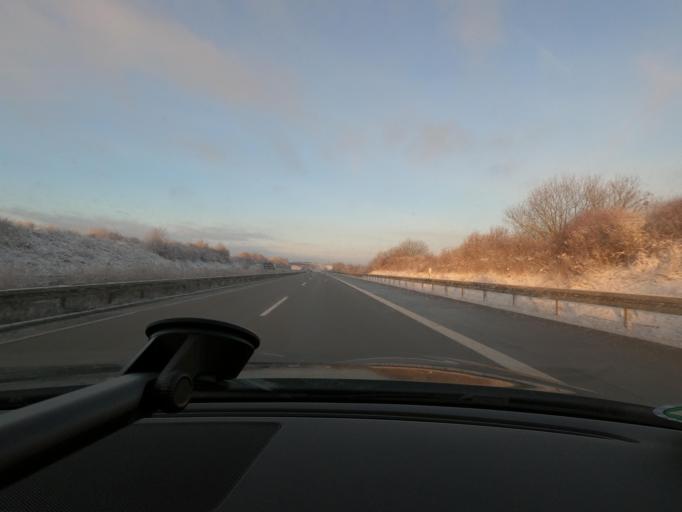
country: DE
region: Thuringia
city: Wingerode
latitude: 51.4026
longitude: 10.2279
